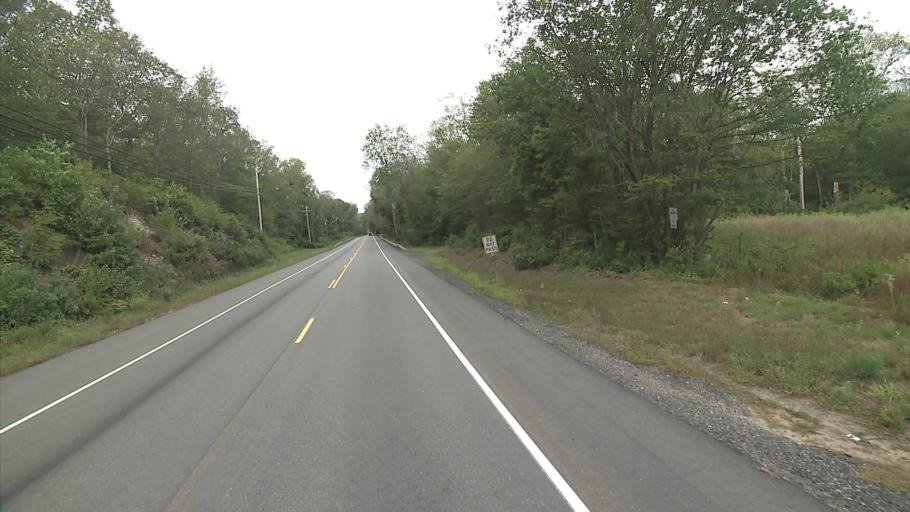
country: US
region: Connecticut
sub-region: New London County
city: Montville Center
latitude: 41.4684
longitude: -72.2563
